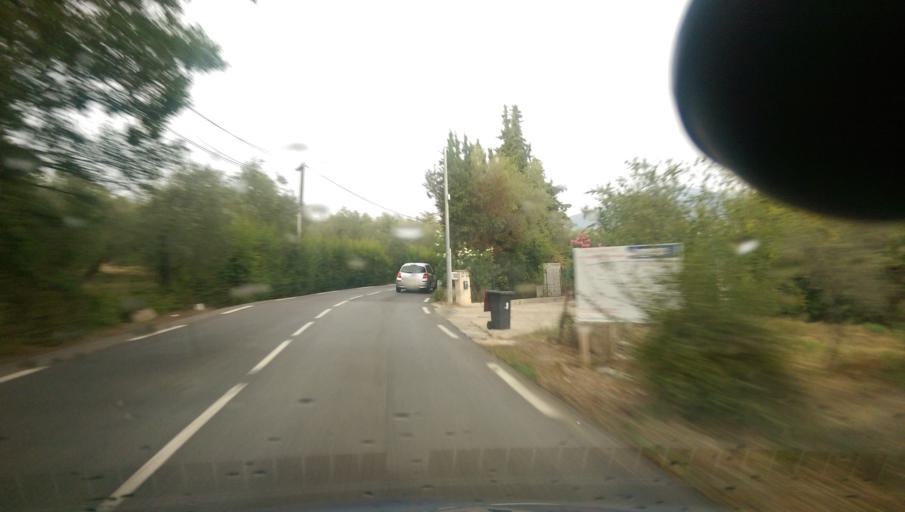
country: FR
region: Provence-Alpes-Cote d'Azur
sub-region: Departement des Alpes-Maritimes
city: Valbonne
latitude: 43.6511
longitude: 7.0101
